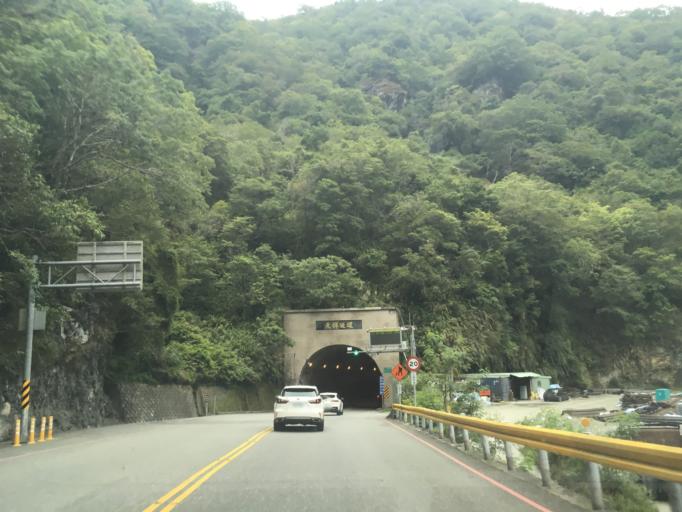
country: TW
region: Taiwan
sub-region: Hualien
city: Hualian
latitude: 24.1824
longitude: 121.4966
